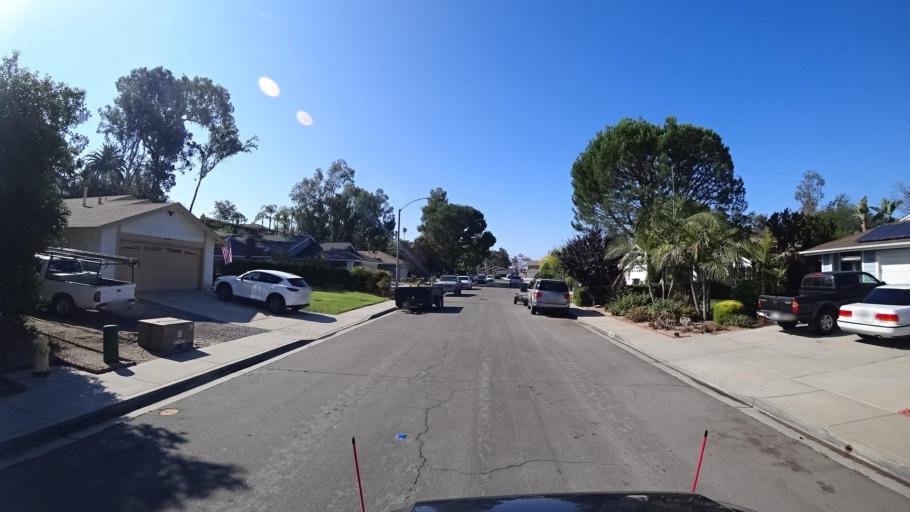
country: US
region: California
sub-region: San Diego County
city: Fallbrook
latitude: 33.3719
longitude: -117.2470
